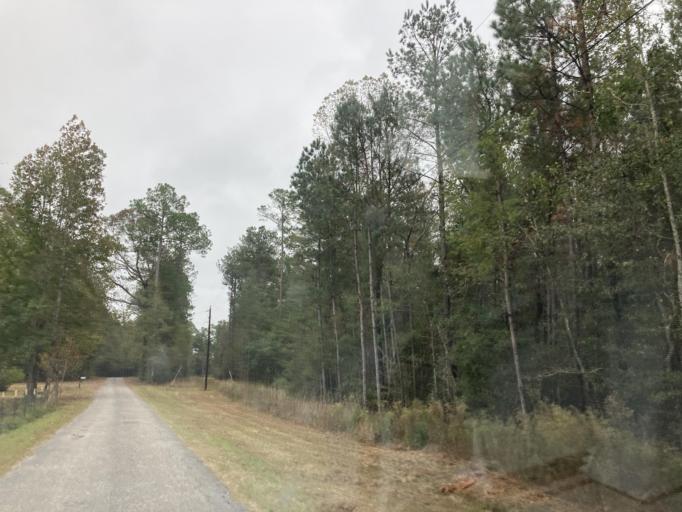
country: US
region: Mississippi
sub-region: Lamar County
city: Purvis
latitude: 31.1979
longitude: -89.4526
